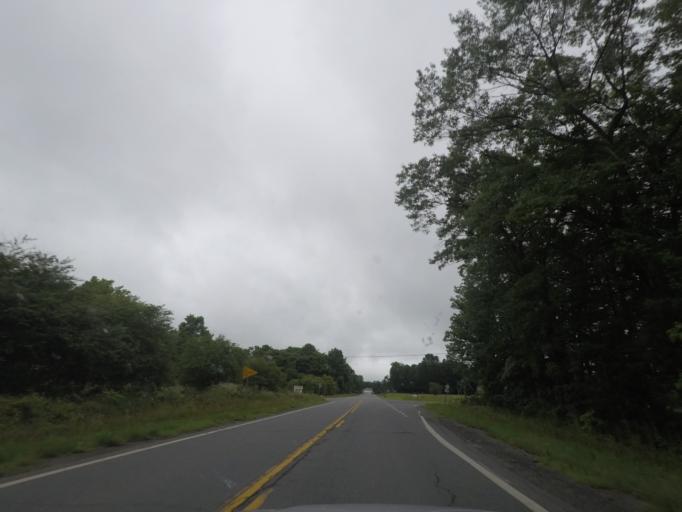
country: US
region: Virginia
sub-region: Fluvanna County
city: Weber City
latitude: 37.6906
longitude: -78.3263
